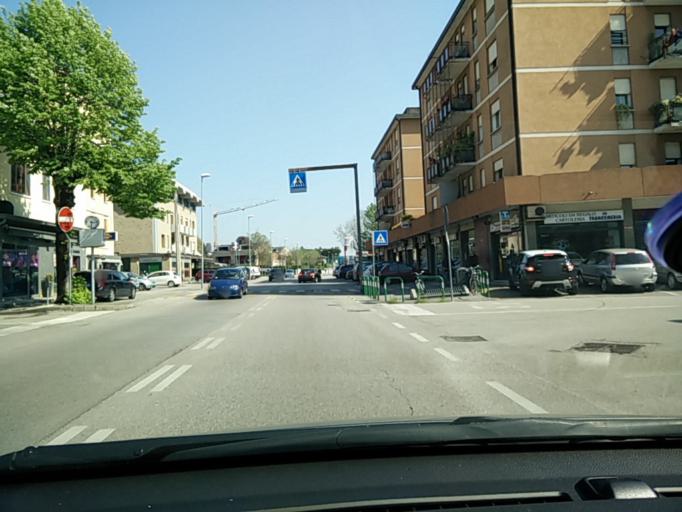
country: IT
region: Veneto
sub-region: Provincia di Padova
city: Noventa
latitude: 45.4220
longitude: 11.9438
